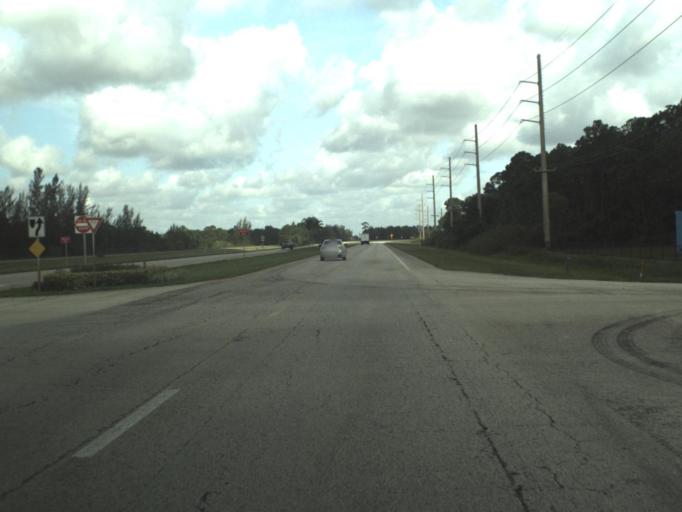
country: US
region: Florida
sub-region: Palm Beach County
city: Limestone Creek
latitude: 26.8938
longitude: -80.2777
